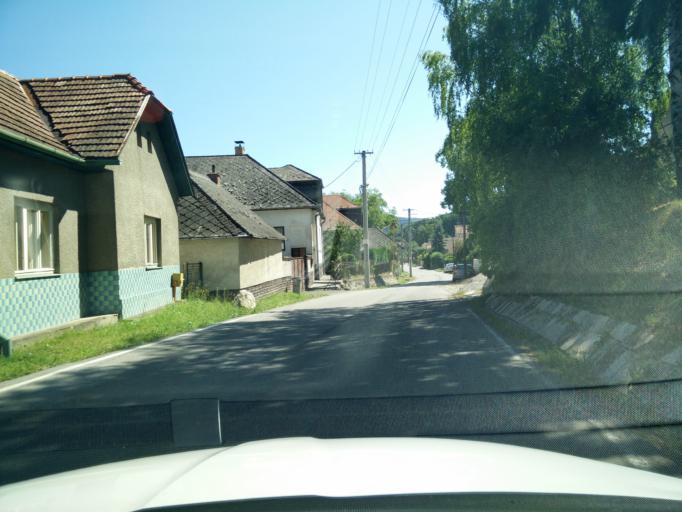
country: SK
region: Nitriansky
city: Prievidza
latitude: 48.7972
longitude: 18.6998
